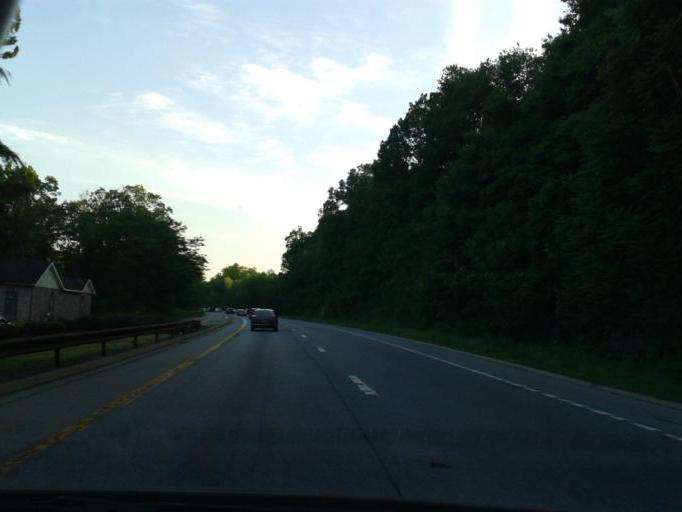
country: US
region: New York
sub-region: Westchester County
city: Harrison
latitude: 40.9936
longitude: -73.7320
